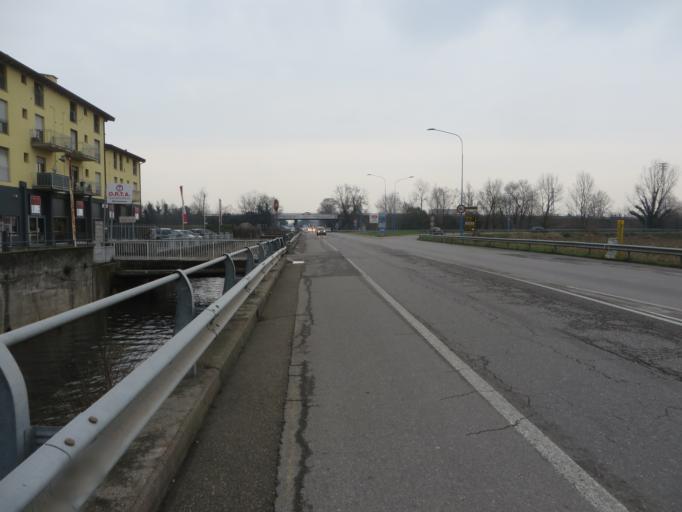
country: IT
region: Lombardy
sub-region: Provincia di Brescia
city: Buffalora-Bettole
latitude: 45.5194
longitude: 10.2815
